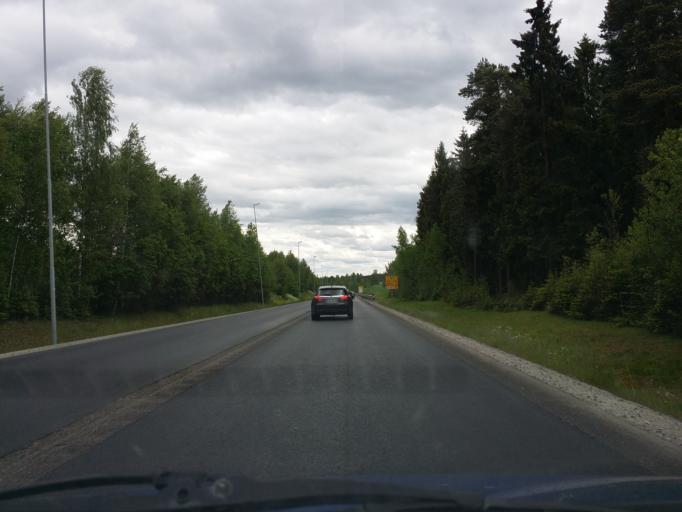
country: NO
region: Hedmark
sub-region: Hamar
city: Hamar
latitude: 60.8382
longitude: 11.0695
